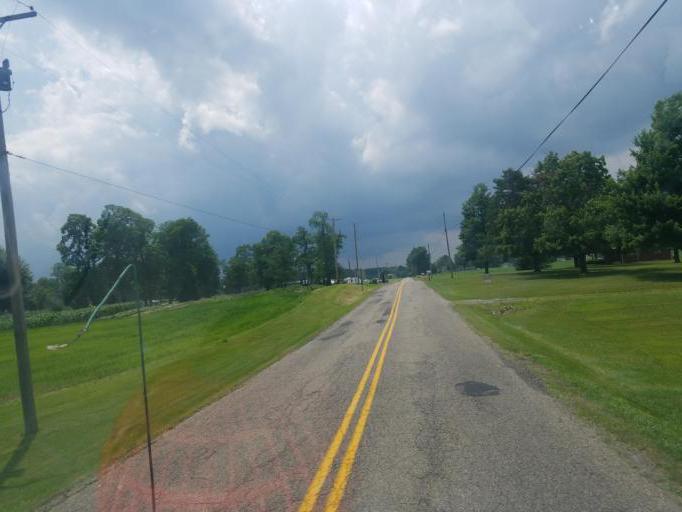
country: US
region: Ohio
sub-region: Columbiana County
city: Salem
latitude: 40.9739
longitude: -80.9085
